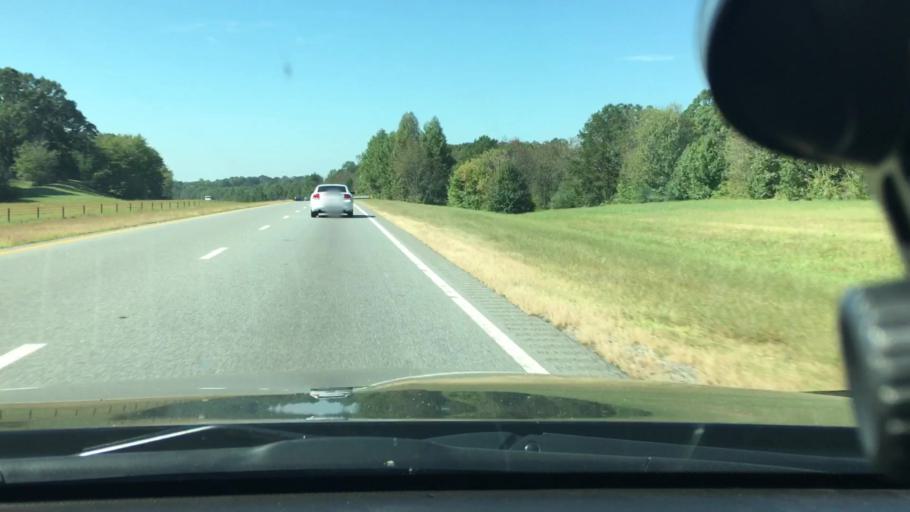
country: US
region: North Carolina
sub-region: Cleveland County
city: White Plains
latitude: 35.2548
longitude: -81.3927
